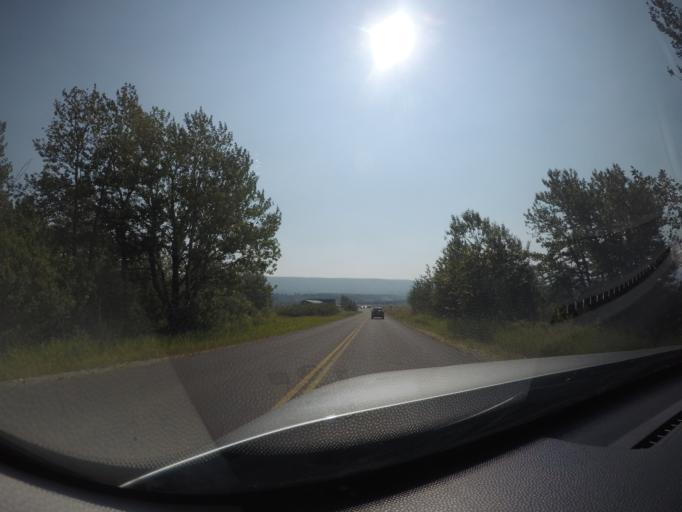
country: US
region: Montana
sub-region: Glacier County
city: North Browning
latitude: 48.7488
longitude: -113.4428
